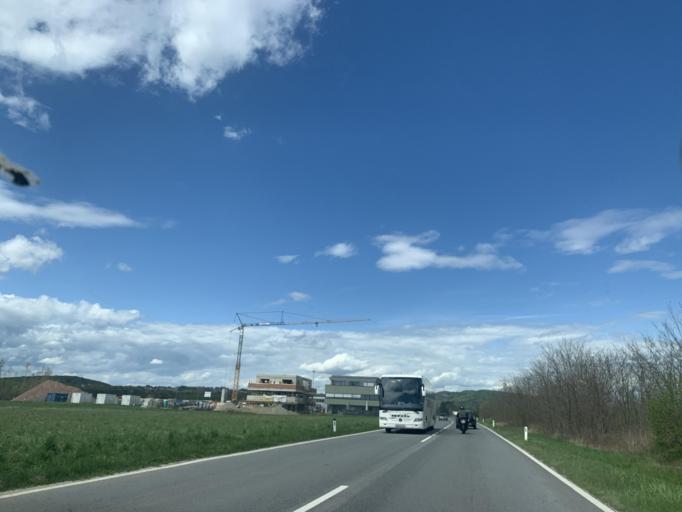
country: AT
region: Styria
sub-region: Politischer Bezirk Leibnitz
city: Kaindorf an der Sulm
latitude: 46.8170
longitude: 15.5256
